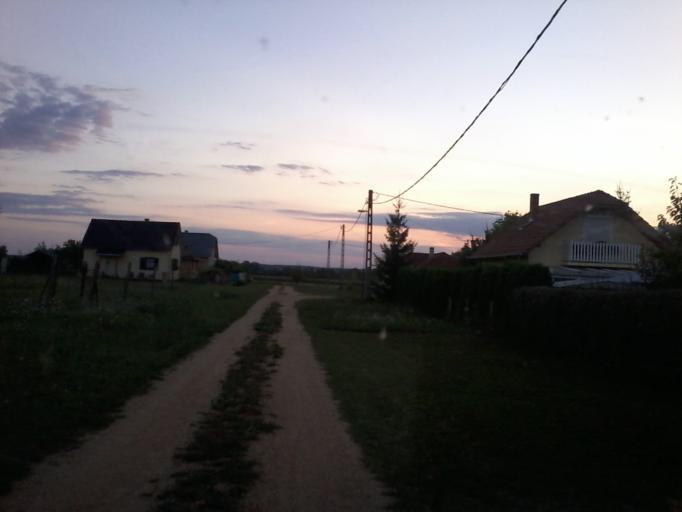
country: HU
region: Vas
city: Janoshaza
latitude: 47.1611
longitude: 17.0959
